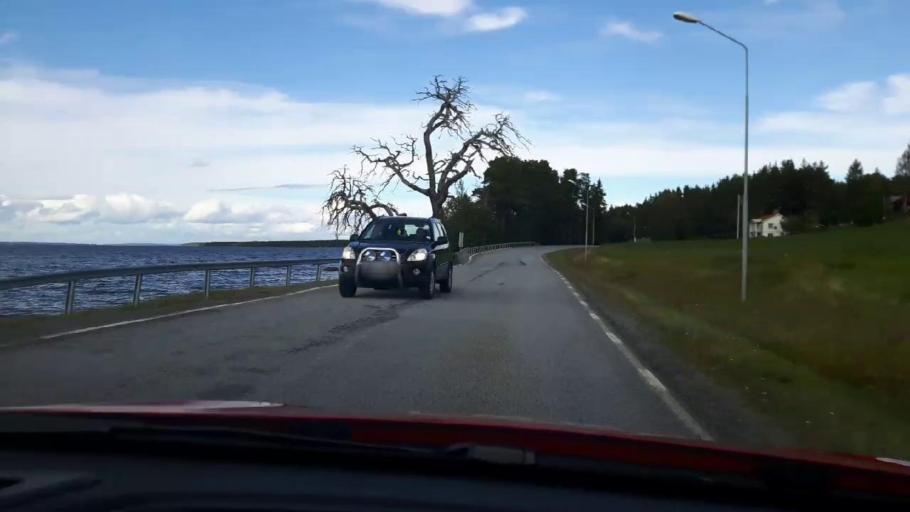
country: SE
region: Jaemtland
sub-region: Bergs Kommun
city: Hoverberg
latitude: 62.9829
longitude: 14.4807
